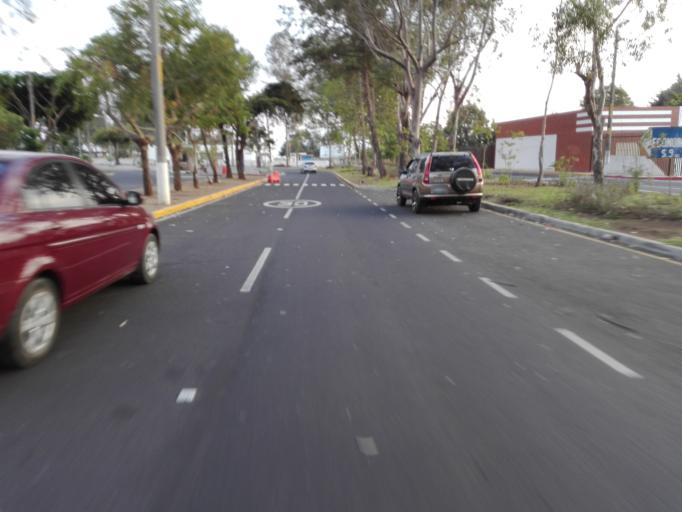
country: GT
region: Guatemala
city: Santa Catarina Pinula
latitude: 14.5828
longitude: -90.5568
